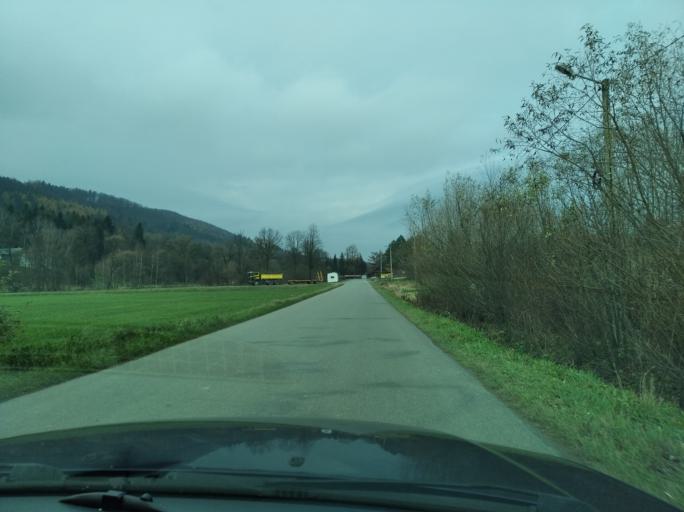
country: PL
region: Subcarpathian Voivodeship
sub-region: Powiat krosnienski
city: Odrzykon
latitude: 49.7817
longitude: 21.7631
